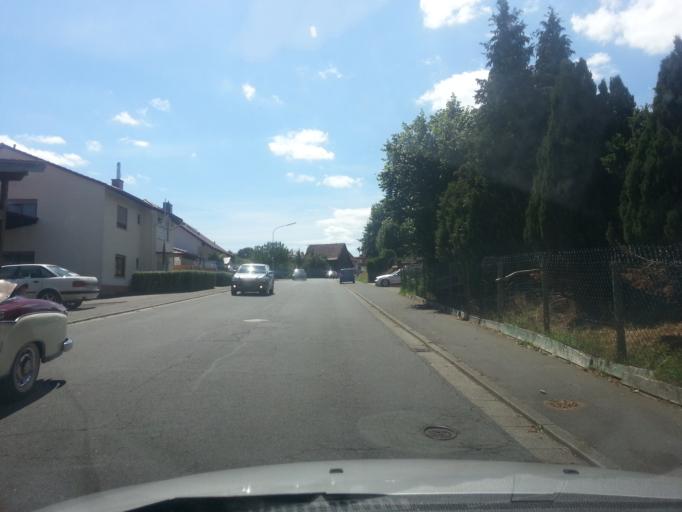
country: DE
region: Hesse
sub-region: Regierungsbezirk Darmstadt
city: Bad Konig
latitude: 49.7255
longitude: 8.9609
